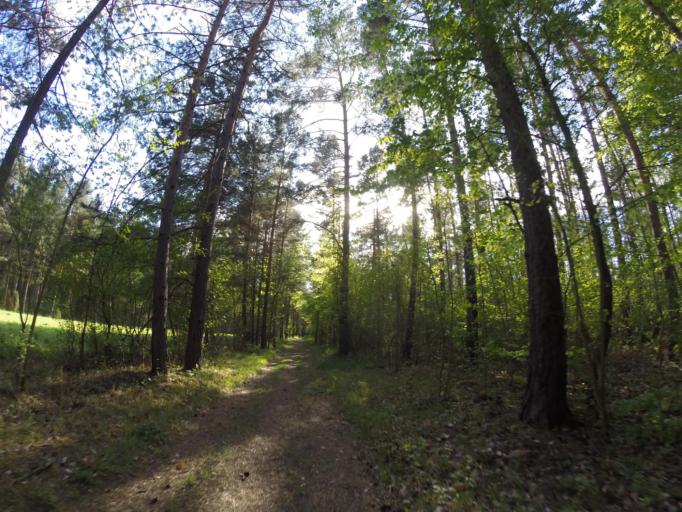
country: DE
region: Thuringia
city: Sulza
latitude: 50.9017
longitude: 11.6216
